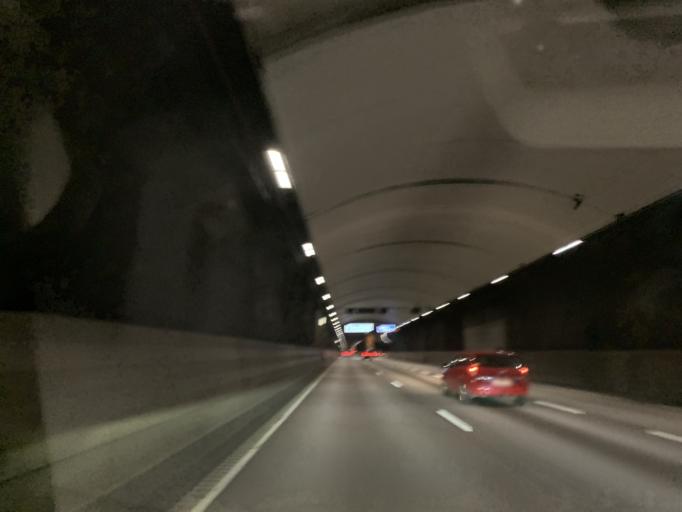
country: SE
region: Stockholm
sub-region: Stockholms Kommun
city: Arsta
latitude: 59.2961
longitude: 18.0472
